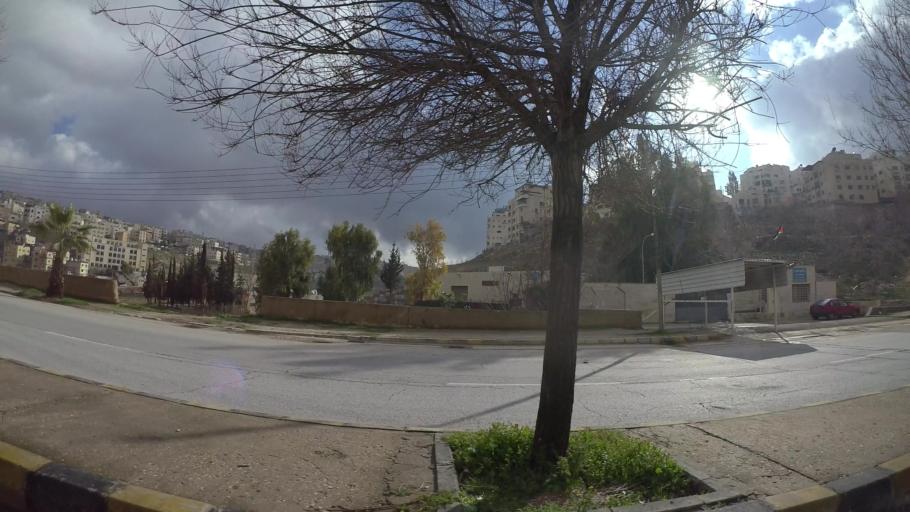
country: JO
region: Amman
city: Amman
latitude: 31.9409
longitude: 35.9001
